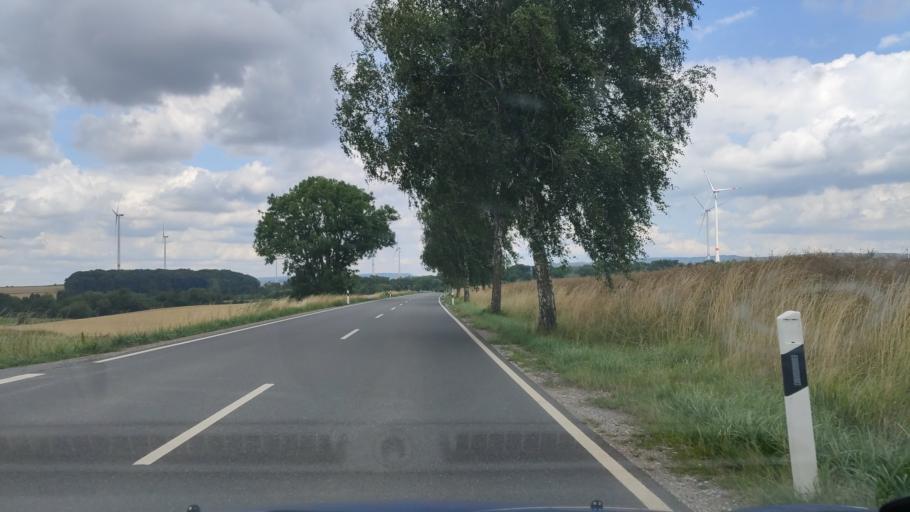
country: DE
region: Lower Saxony
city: Coppenbrugge
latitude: 52.1088
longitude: 9.5009
